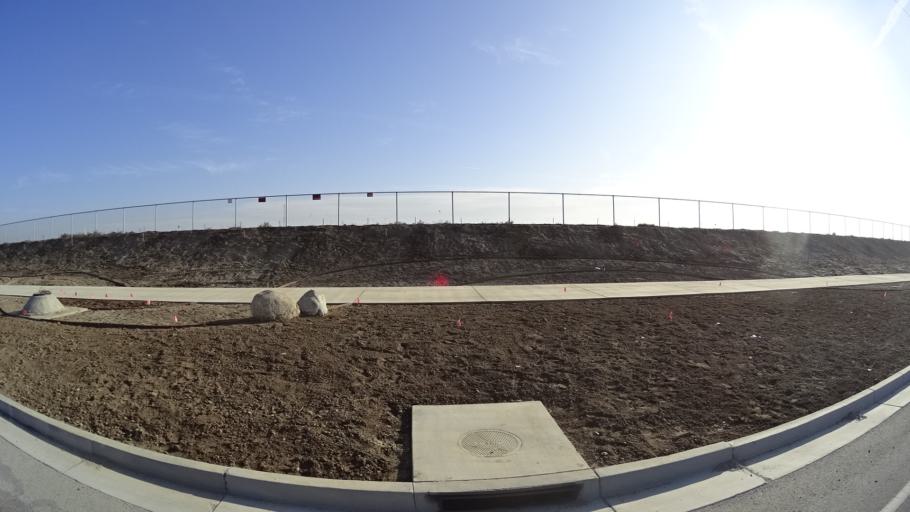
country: US
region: California
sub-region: Kern County
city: Greenfield
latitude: 35.2777
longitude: -119.0920
